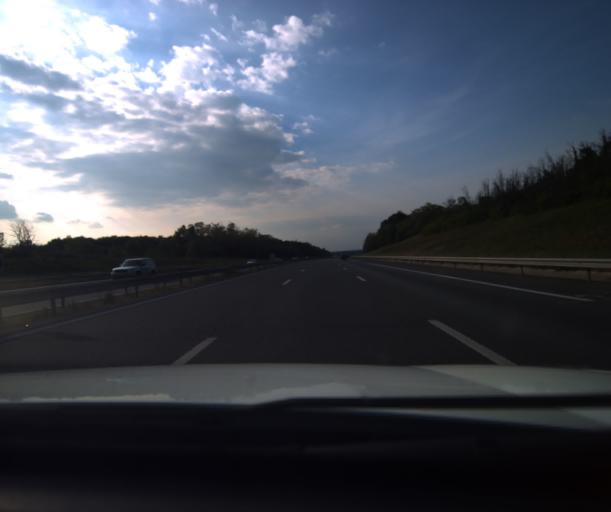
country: FR
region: Midi-Pyrenees
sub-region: Departement de la Haute-Garonne
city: Castelnau-d'Estretefonds
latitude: 43.7995
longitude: 1.3713
